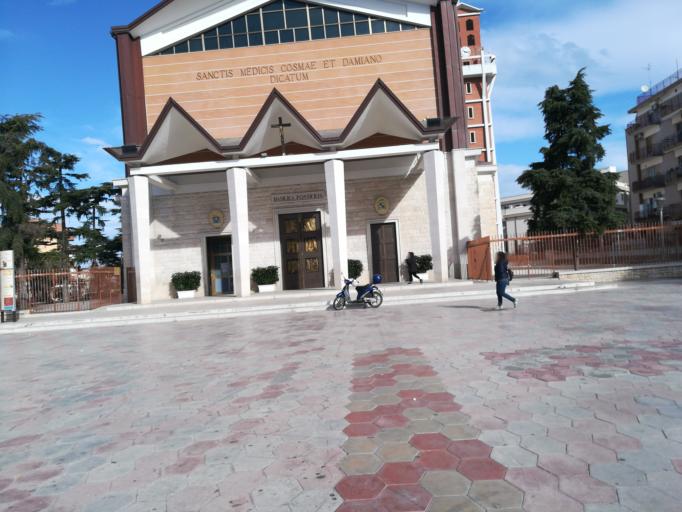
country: IT
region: Apulia
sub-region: Provincia di Bari
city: Bitonto
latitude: 41.1139
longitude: 16.6916
